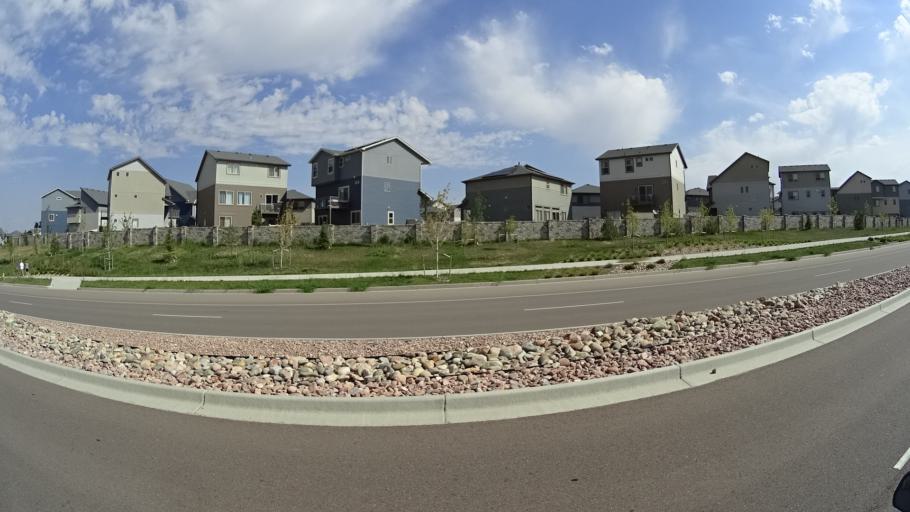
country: US
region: Colorado
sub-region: El Paso County
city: Cimarron Hills
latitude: 38.9266
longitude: -104.6616
